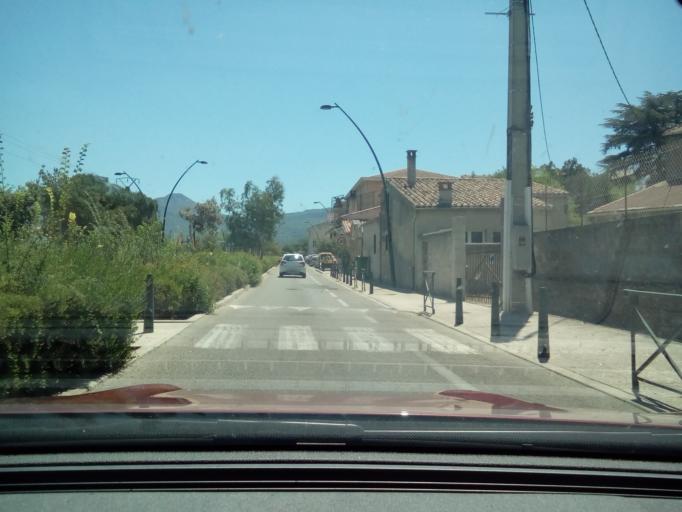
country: FR
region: Provence-Alpes-Cote d'Azur
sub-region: Departement des Bouches-du-Rhone
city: Trets
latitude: 43.4509
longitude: 5.6746
